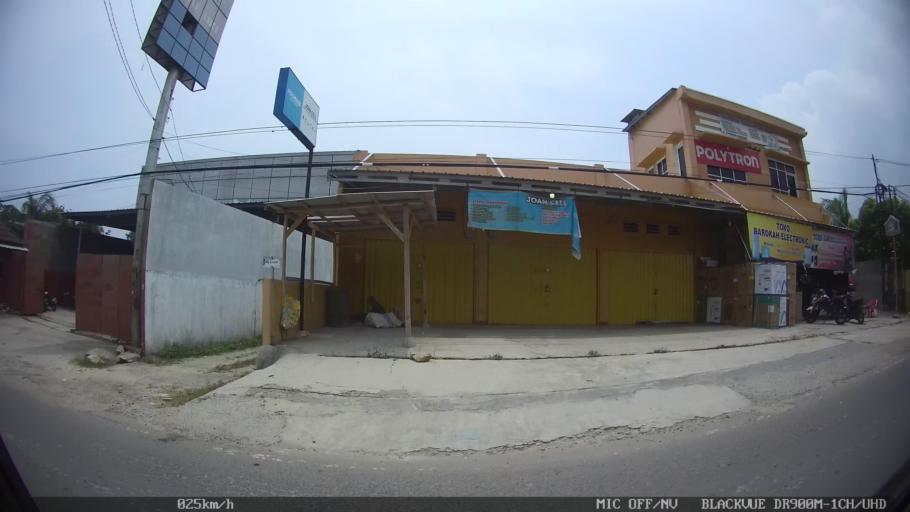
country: ID
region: Lampung
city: Kedaton
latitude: -5.4001
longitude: 105.3097
